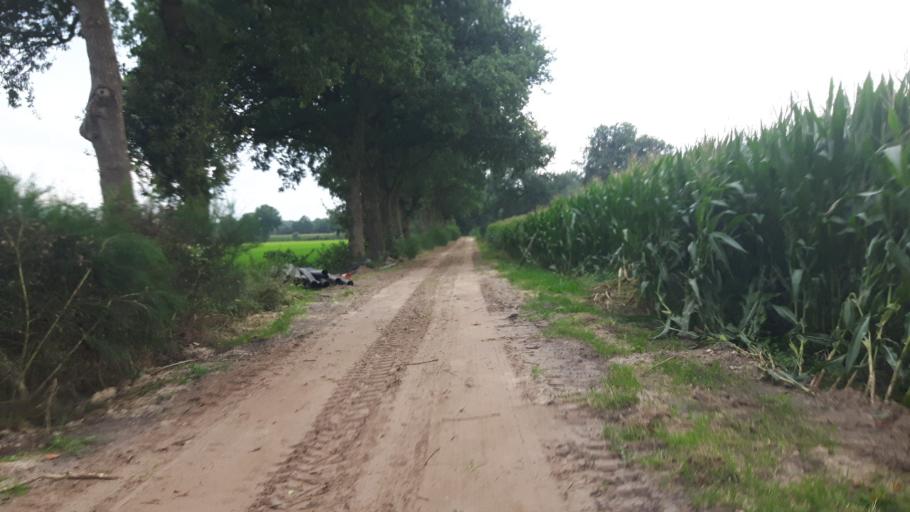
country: NL
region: Friesland
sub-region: Gemeente Heerenveen
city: Jubbega
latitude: 52.9754
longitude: 6.2272
